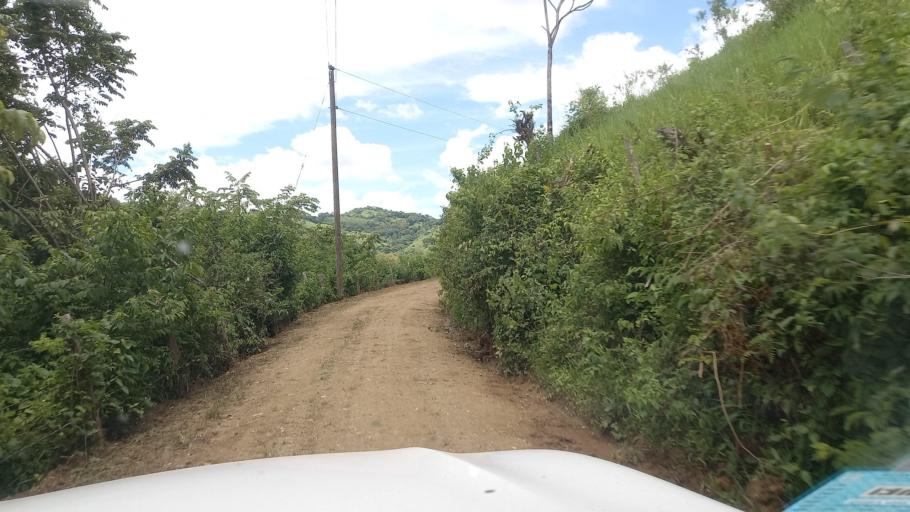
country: NI
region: Nueva Segovia
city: Wiwili
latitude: 13.7326
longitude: -85.7884
